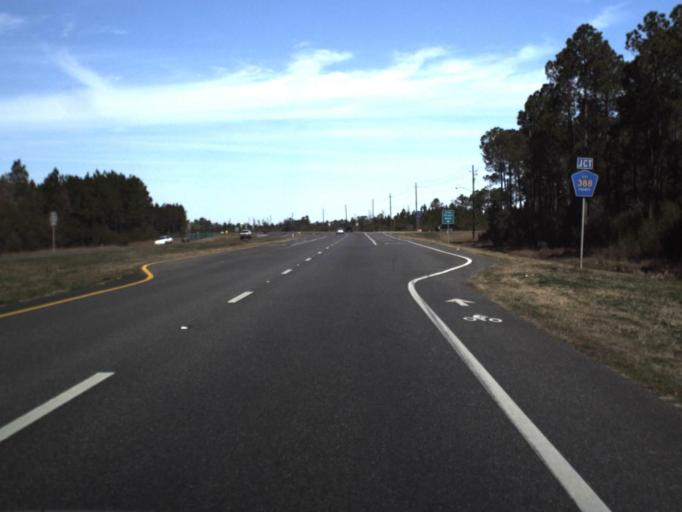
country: US
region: Florida
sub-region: Bay County
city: Lynn Haven
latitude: 30.3340
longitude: -85.6600
